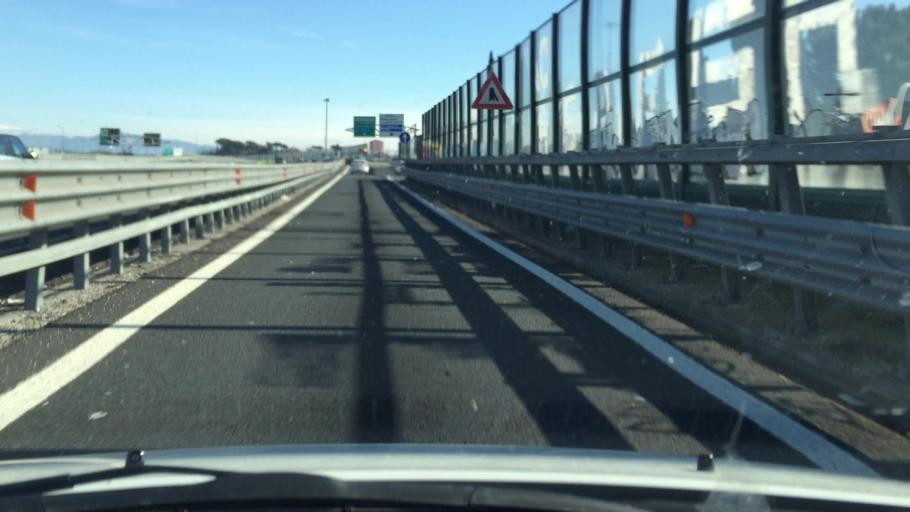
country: IT
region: Latium
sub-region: Citta metropolitana di Roma Capitale
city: Monte Caminetto
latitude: 41.9856
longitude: 12.4910
